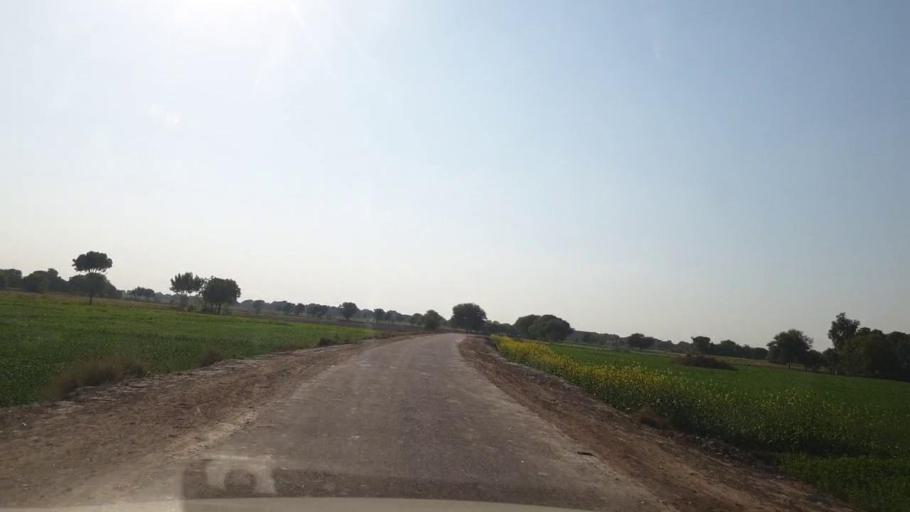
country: PK
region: Sindh
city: Tando Allahyar
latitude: 25.4953
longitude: 68.6524
